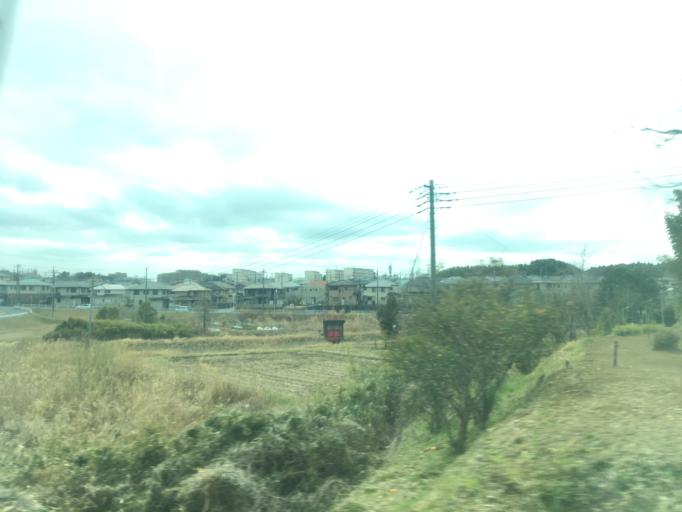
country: JP
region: Chiba
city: Narita
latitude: 35.7878
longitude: 140.3025
